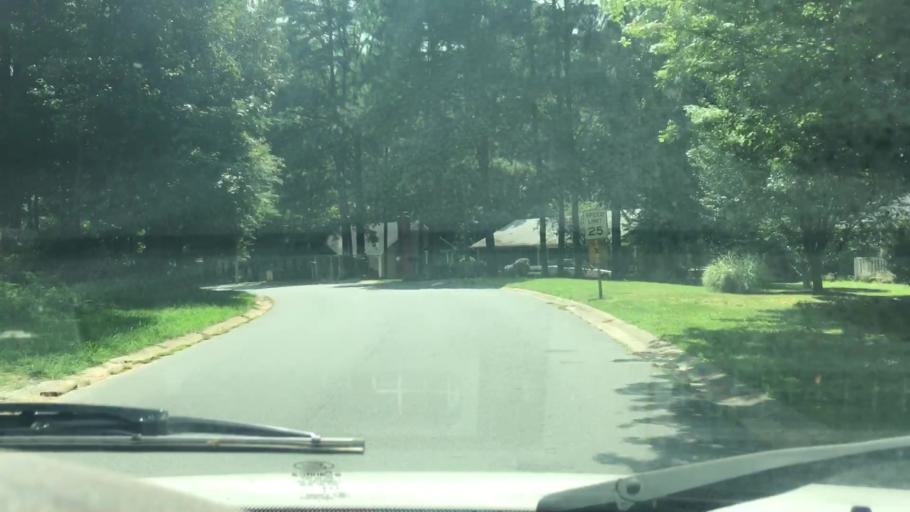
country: US
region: North Carolina
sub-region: Mecklenburg County
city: Cornelius
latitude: 35.4729
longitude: -80.8707
